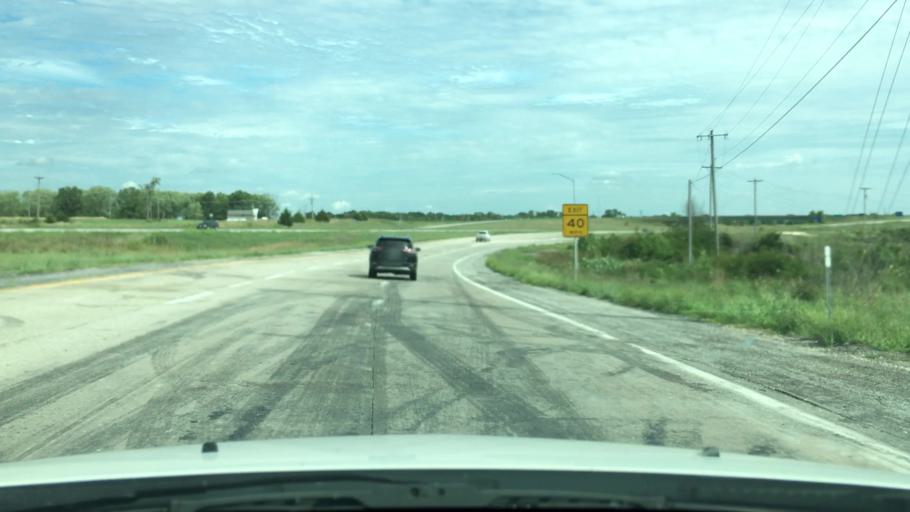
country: US
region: Missouri
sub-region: Audrain County
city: Mexico
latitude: 39.1134
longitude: -91.8948
